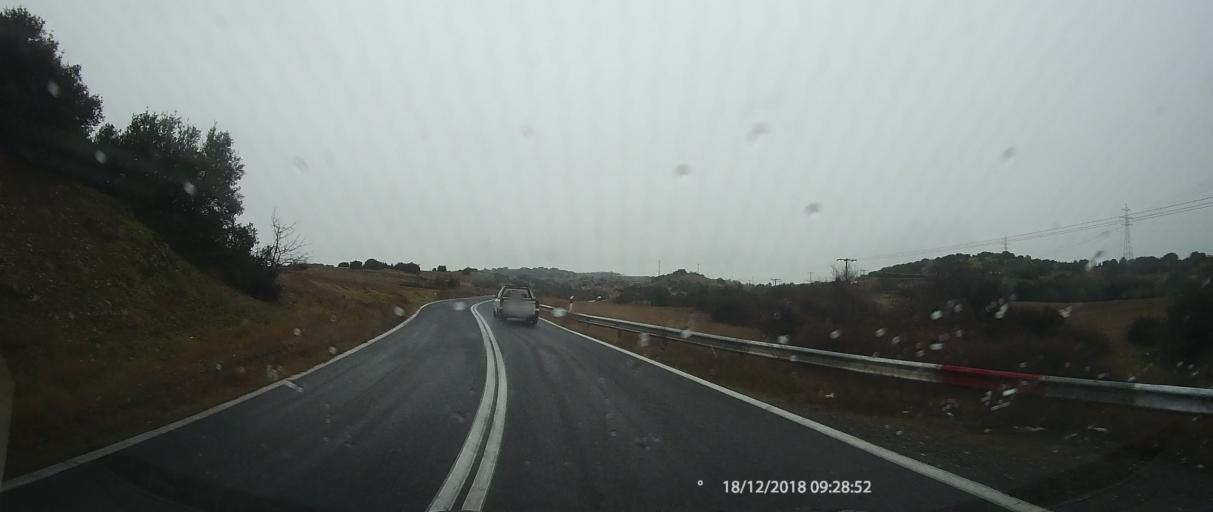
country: GR
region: Thessaly
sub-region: Nomos Larisis
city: Elassona
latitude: 39.9229
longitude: 22.1720
